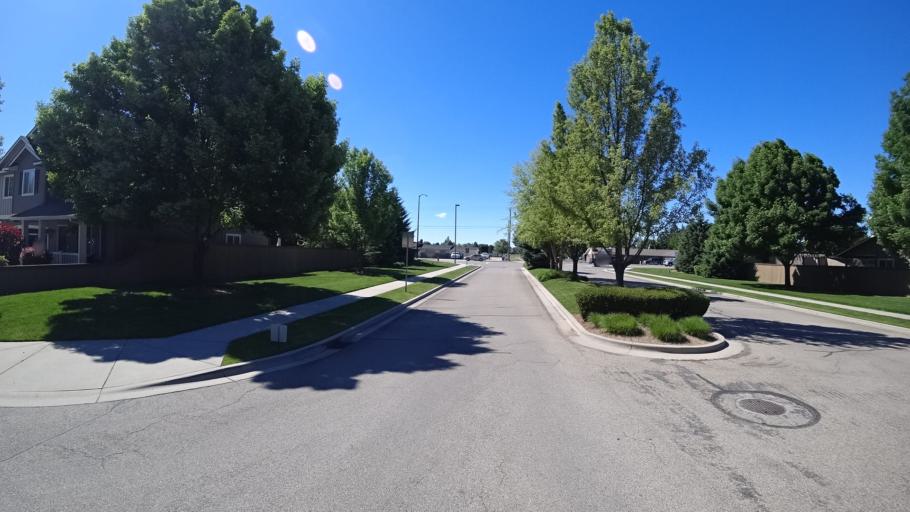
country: US
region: Idaho
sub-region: Ada County
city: Meridian
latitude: 43.6344
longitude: -116.3907
